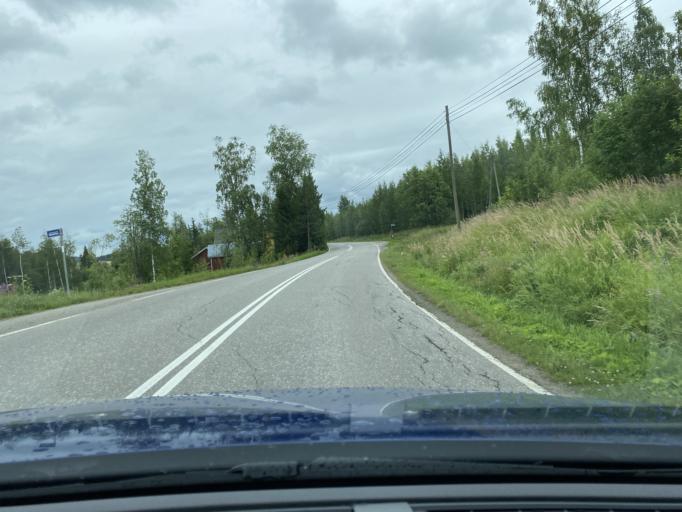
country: FI
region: Pirkanmaa
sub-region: Lounais-Pirkanmaa
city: Punkalaidun
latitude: 61.0938
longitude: 23.1428
